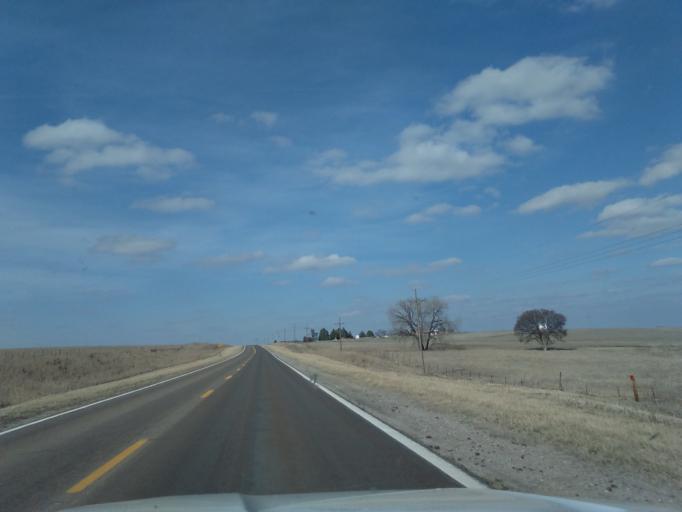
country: US
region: Nebraska
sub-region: Jefferson County
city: Fairbury
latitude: 40.0773
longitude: -96.9352
